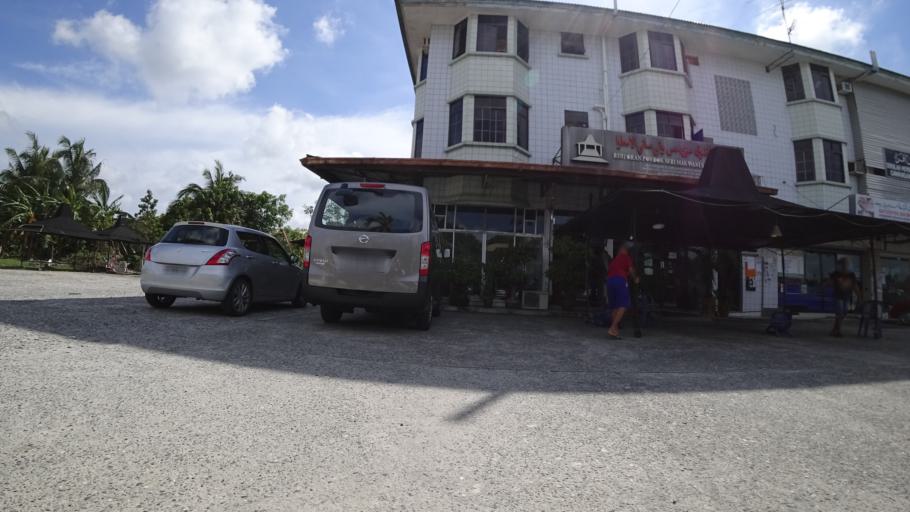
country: BN
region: Brunei and Muara
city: Bandar Seri Begawan
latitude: 4.8873
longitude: 114.8429
